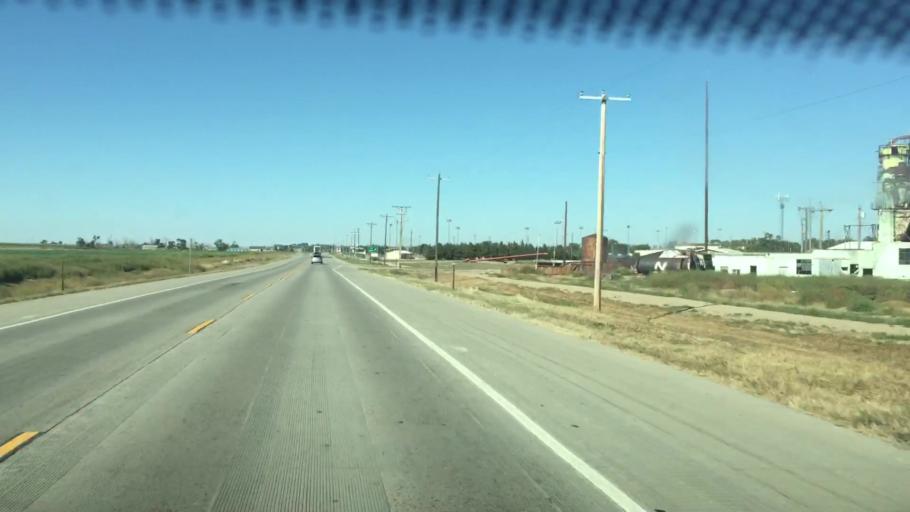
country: US
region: Colorado
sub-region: Prowers County
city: Lamar
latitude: 38.1508
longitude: -102.7234
